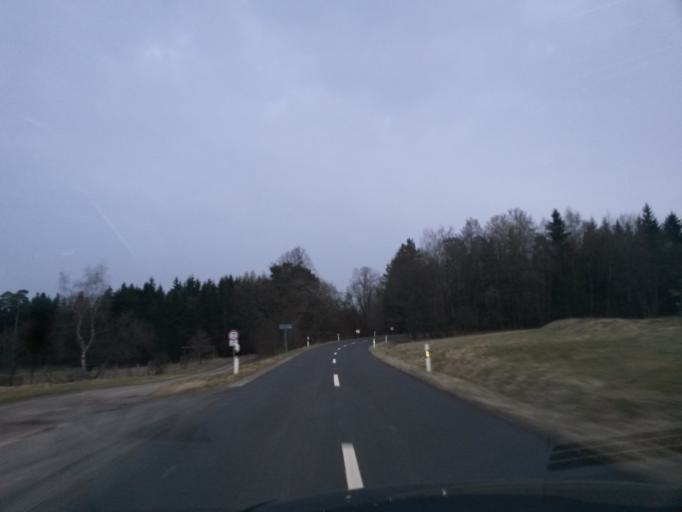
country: DE
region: Bavaria
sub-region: Regierungsbezirk Unterfranken
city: Bad Konigshofen im Grabfeld
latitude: 50.2433
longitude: 10.4610
